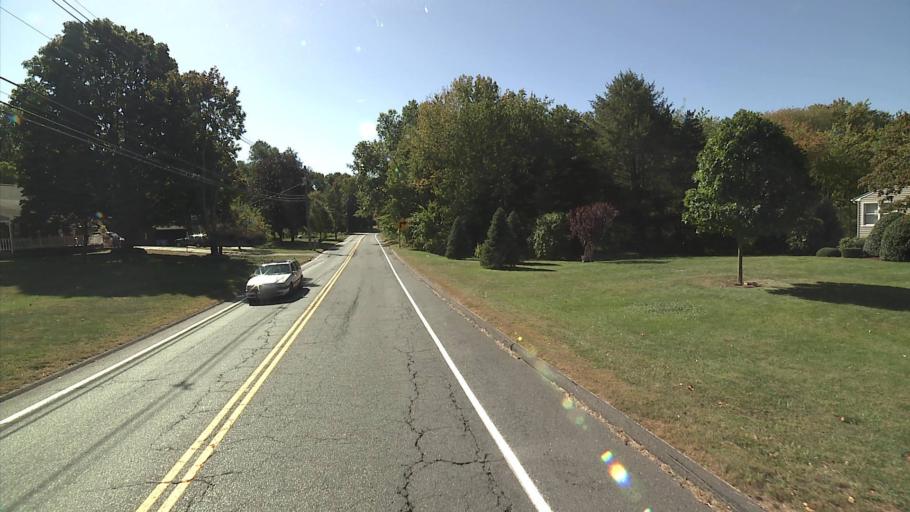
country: US
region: Connecticut
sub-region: Hartford County
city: Bristol
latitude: 41.7131
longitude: -72.9457
